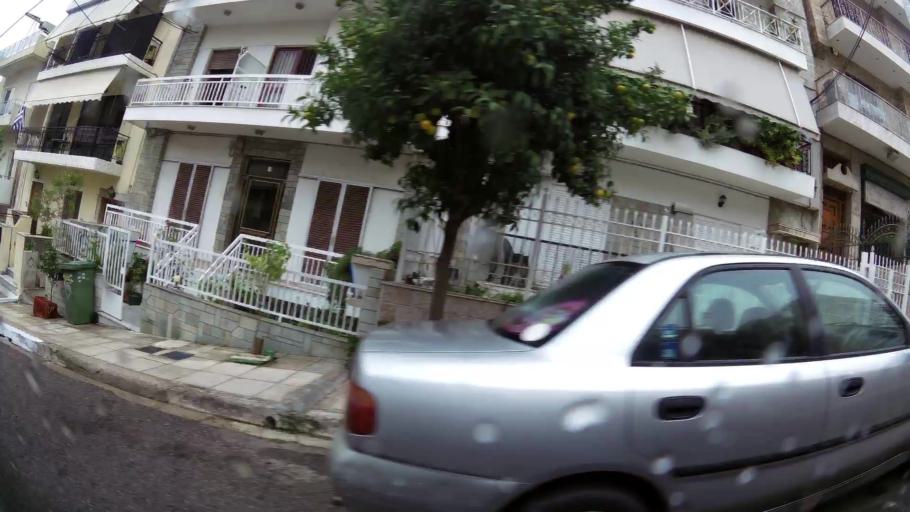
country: GR
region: Attica
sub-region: Nomos Piraios
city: Korydallos
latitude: 37.9869
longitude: 23.6385
